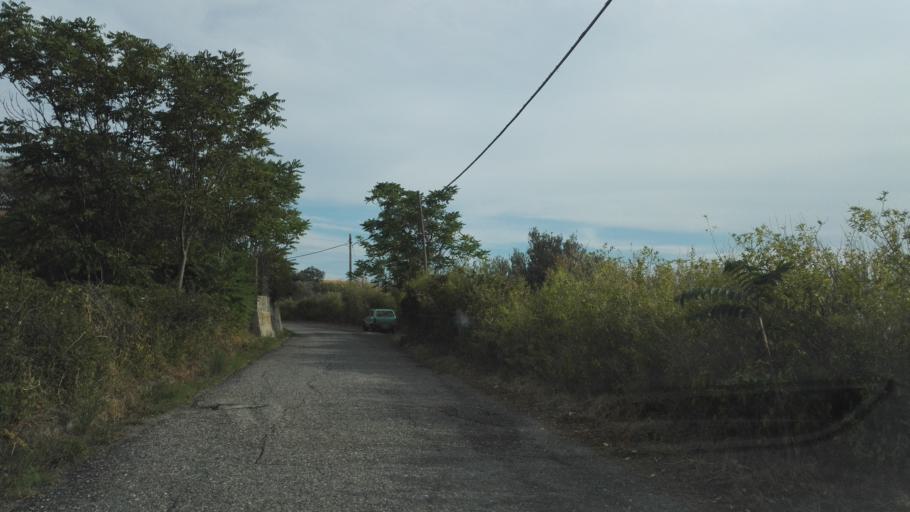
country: IT
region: Calabria
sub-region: Provincia di Reggio Calabria
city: Stignano
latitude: 38.4236
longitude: 16.4652
